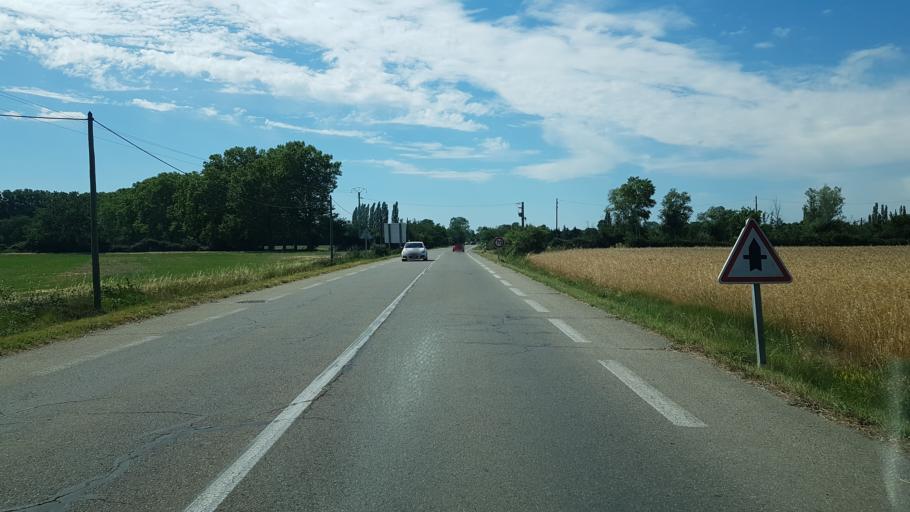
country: FR
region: Provence-Alpes-Cote d'Azur
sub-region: Departement des Bouches-du-Rhone
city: Saint-Martin-de-Crau
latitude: 43.6433
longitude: 4.7991
